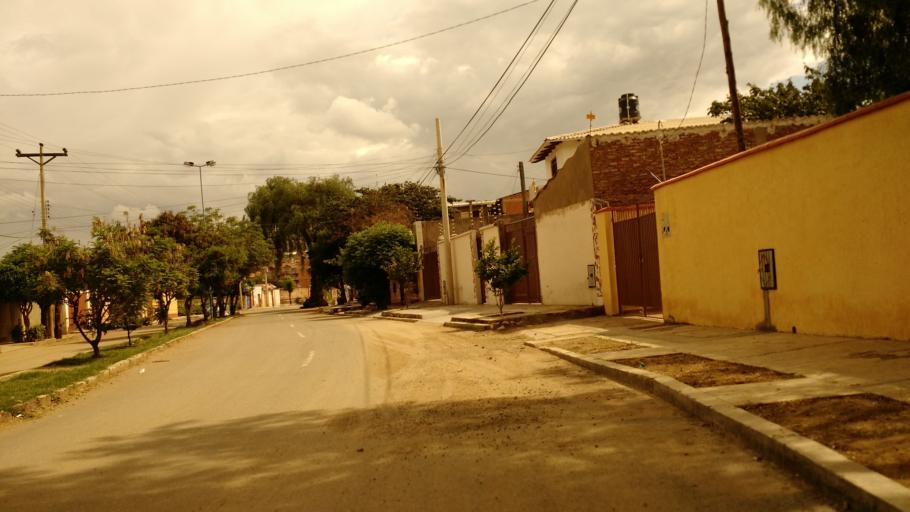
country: BO
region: Cochabamba
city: Cochabamba
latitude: -17.4182
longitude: -66.1240
